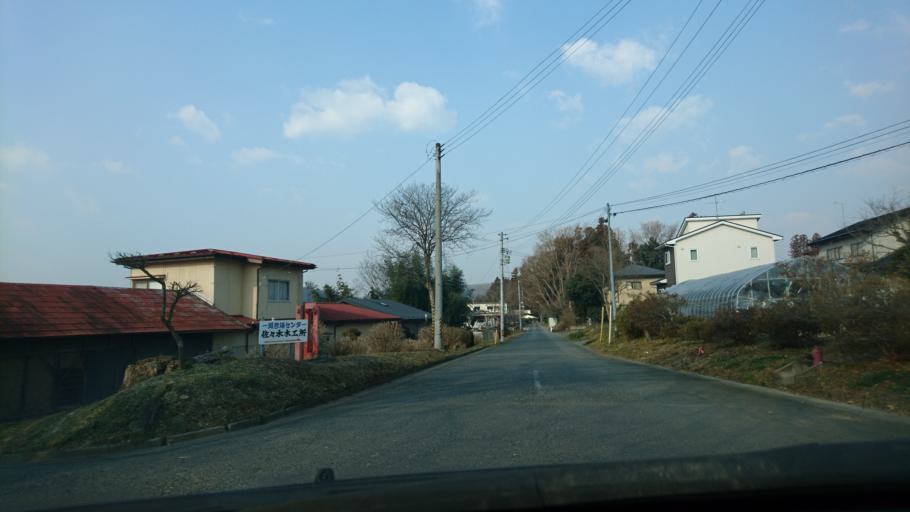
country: JP
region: Iwate
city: Ichinoseki
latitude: 38.9300
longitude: 141.0942
